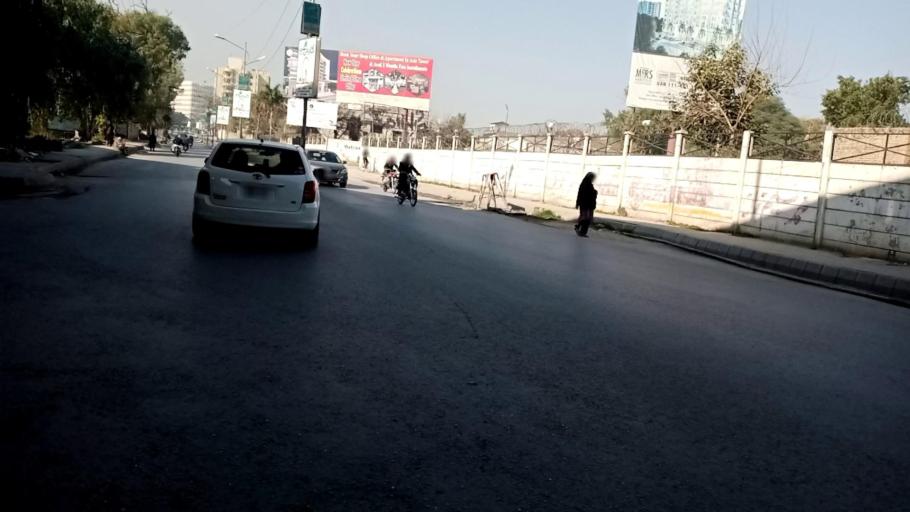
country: PK
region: Khyber Pakhtunkhwa
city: Peshawar
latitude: 34.0029
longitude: 71.5499
